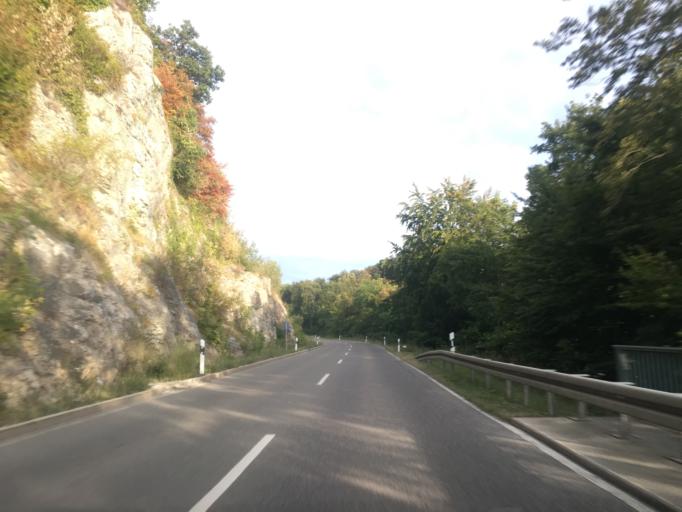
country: DE
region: Baden-Wuerttemberg
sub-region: Tuebingen Region
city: Eningen unter Achalm
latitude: 48.4883
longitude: 9.2908
